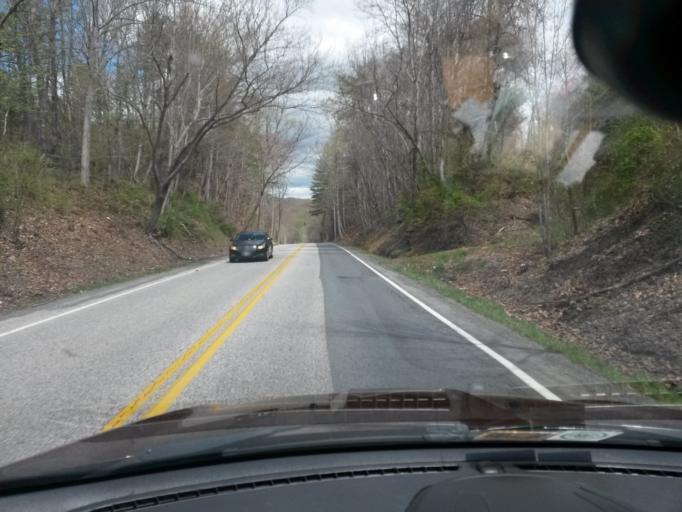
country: US
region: Virginia
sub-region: City of Buena Vista
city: Buena Vista
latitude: 37.6878
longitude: -79.3975
